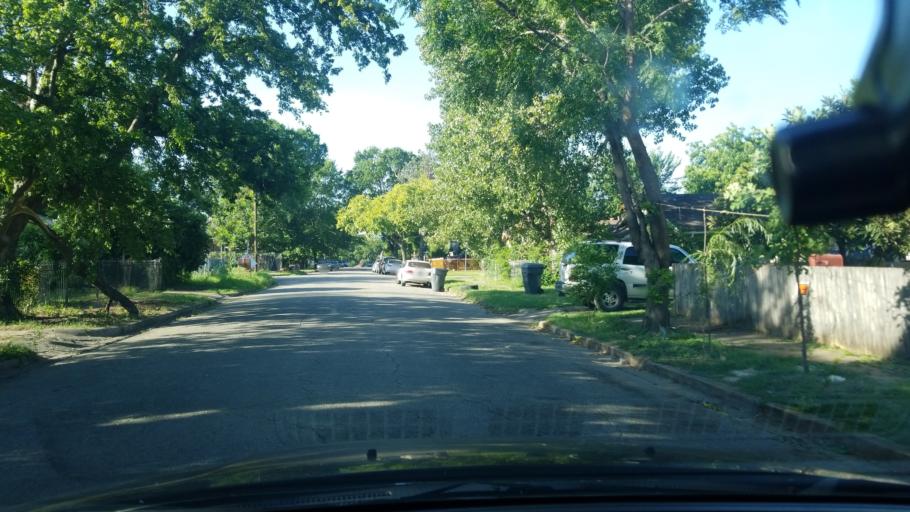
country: US
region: Texas
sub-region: Dallas County
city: Dallas
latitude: 32.7196
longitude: -96.8133
